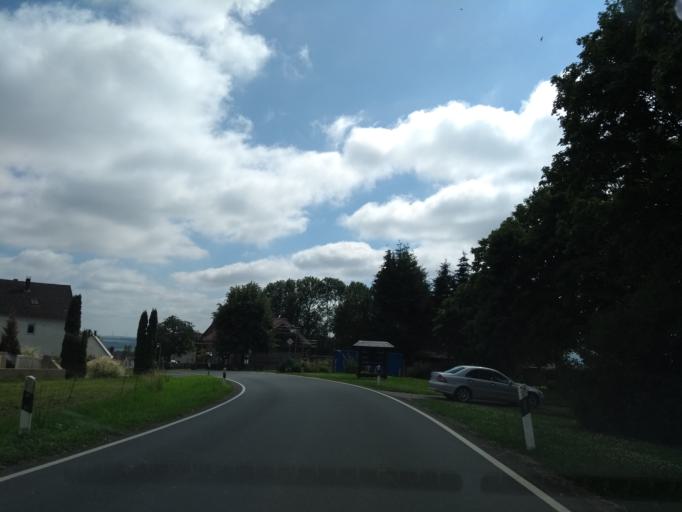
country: DE
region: North Rhine-Westphalia
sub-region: Regierungsbezirk Detmold
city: Lugde
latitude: 51.9519
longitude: 9.2977
